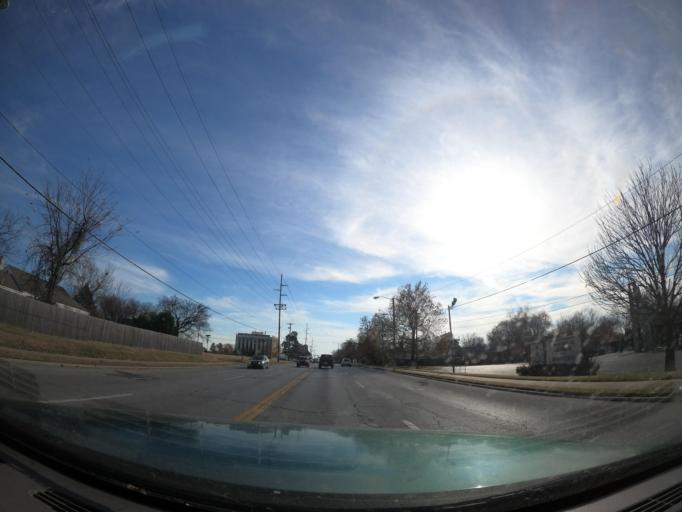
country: US
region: Oklahoma
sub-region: Tulsa County
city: Tulsa
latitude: 36.1305
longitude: -95.9404
